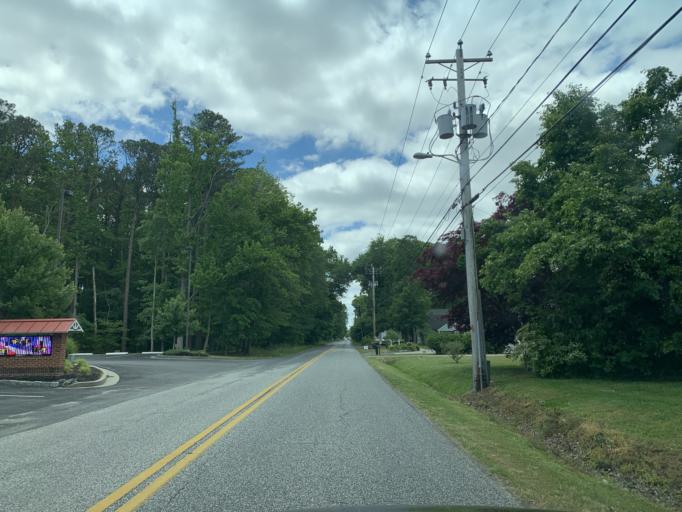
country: US
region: Maryland
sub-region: Worcester County
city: West Ocean City
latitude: 38.3454
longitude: -75.1167
